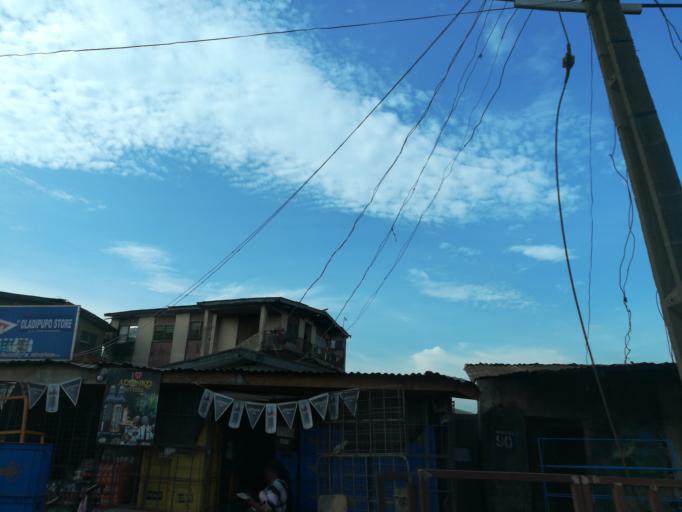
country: NG
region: Lagos
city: Oshodi
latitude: 6.5566
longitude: 3.3419
